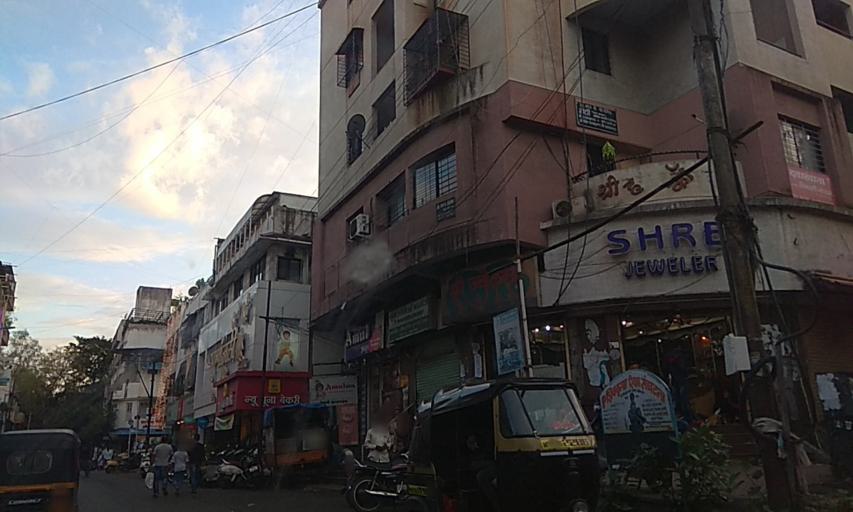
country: IN
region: Maharashtra
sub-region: Pune Division
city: Pune
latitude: 18.4975
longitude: 73.8510
